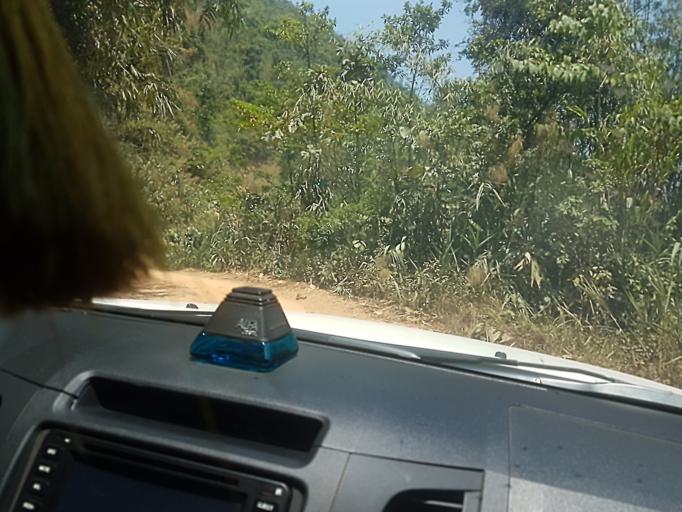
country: VN
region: Nghe An
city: Con Cuong
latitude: 18.6036
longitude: 104.7328
